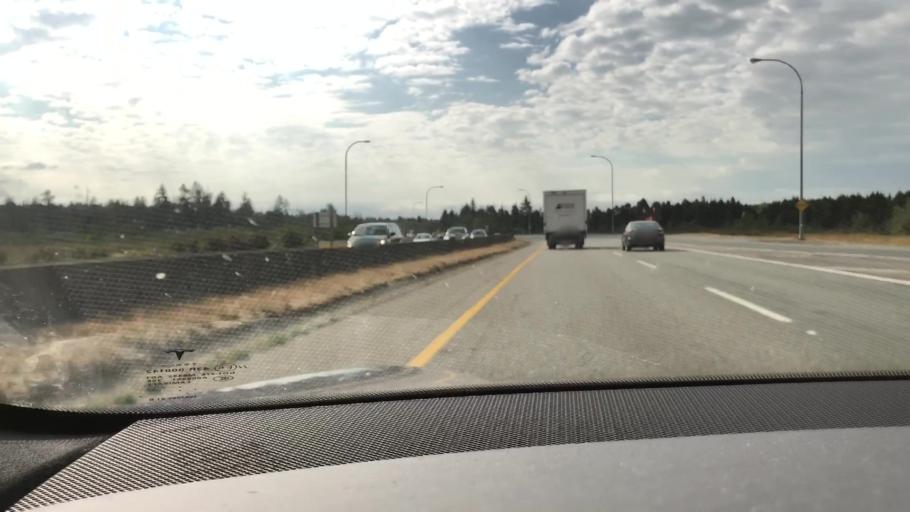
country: CA
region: British Columbia
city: Delta
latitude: 49.1426
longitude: -122.9359
